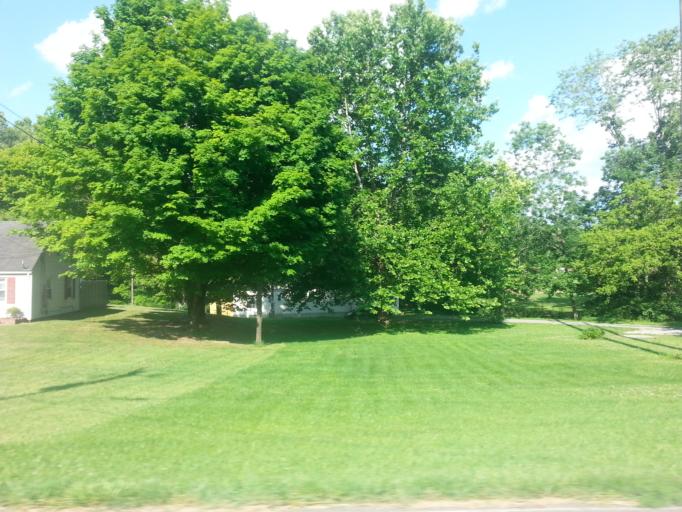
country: US
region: Tennessee
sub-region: Knox County
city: Knoxville
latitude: 36.0766
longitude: -83.8977
